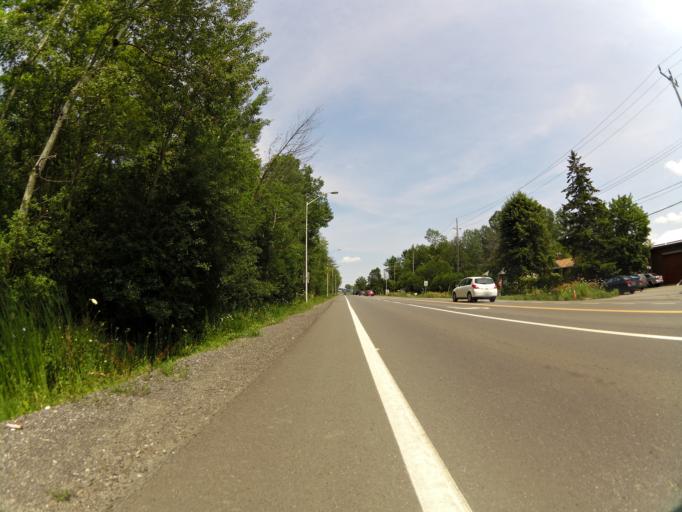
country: CA
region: Ontario
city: Ottawa
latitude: 45.3176
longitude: -75.6301
